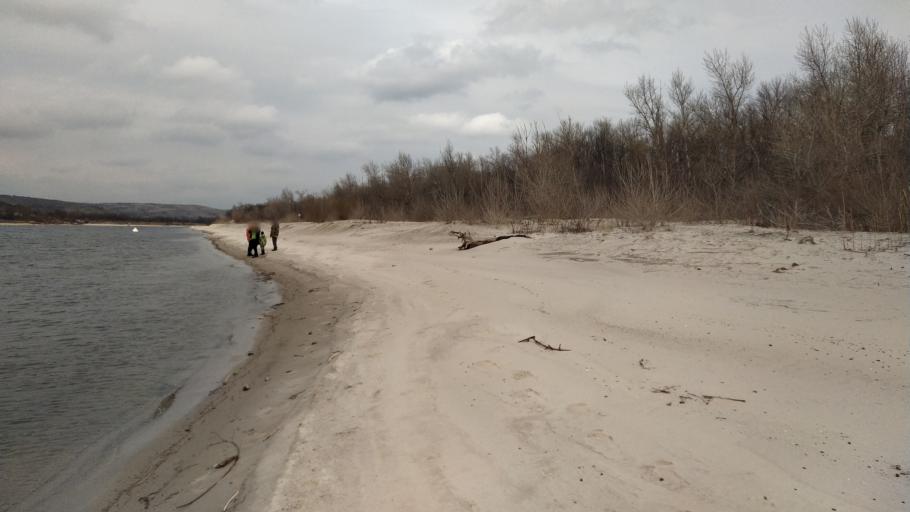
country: RU
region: Rostov
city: Semikarakorsk
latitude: 47.5545
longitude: 40.6723
